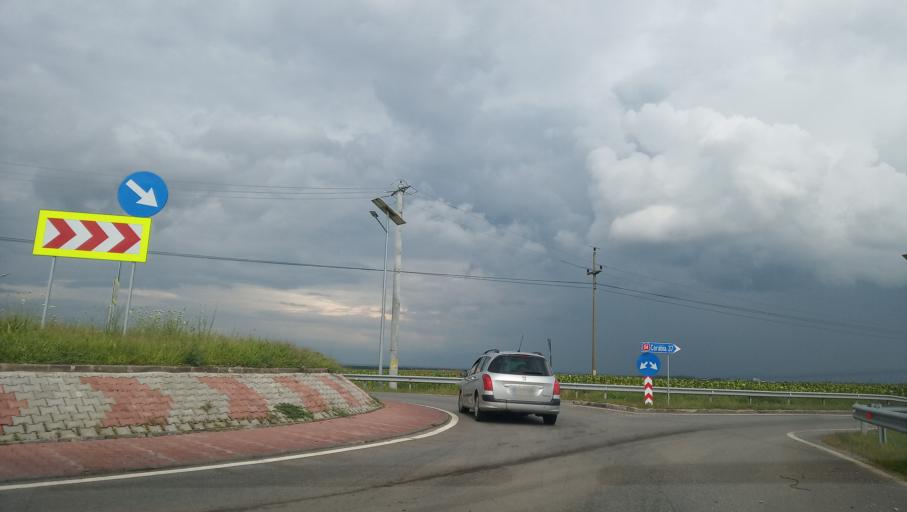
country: RO
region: Olt
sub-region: Comuna Deveselu
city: Comanca
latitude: 44.0896
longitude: 24.3653
